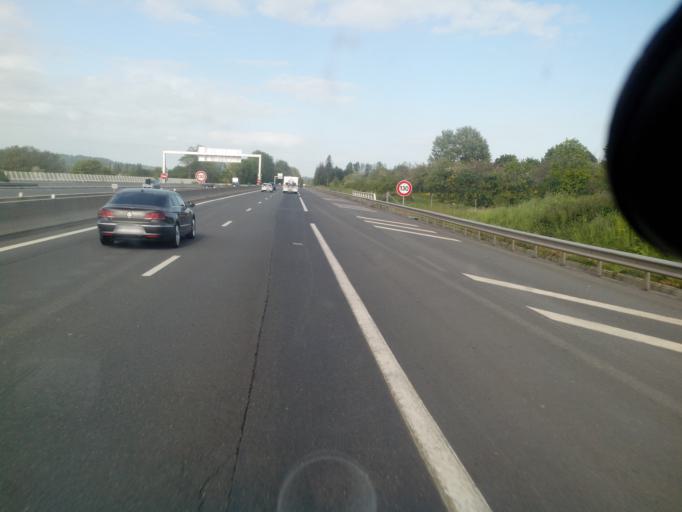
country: FR
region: Lower Normandy
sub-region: Departement du Calvados
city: Dozule
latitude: 49.2311
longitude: -0.0693
